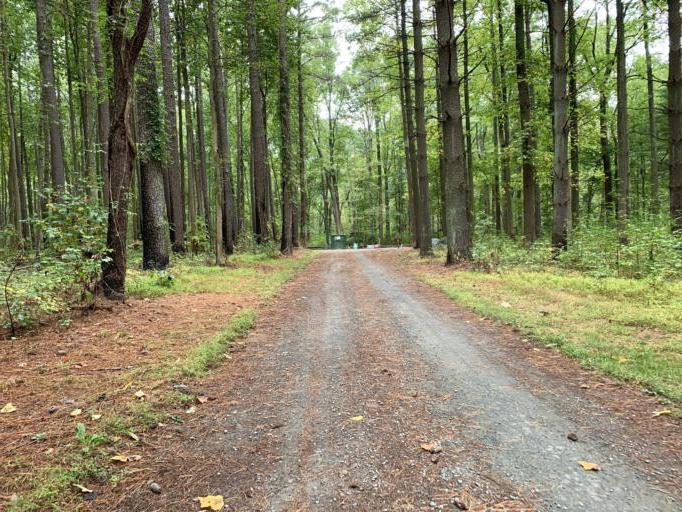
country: US
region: Delaware
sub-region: New Castle County
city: Townsend
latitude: 39.3446
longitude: -75.6746
